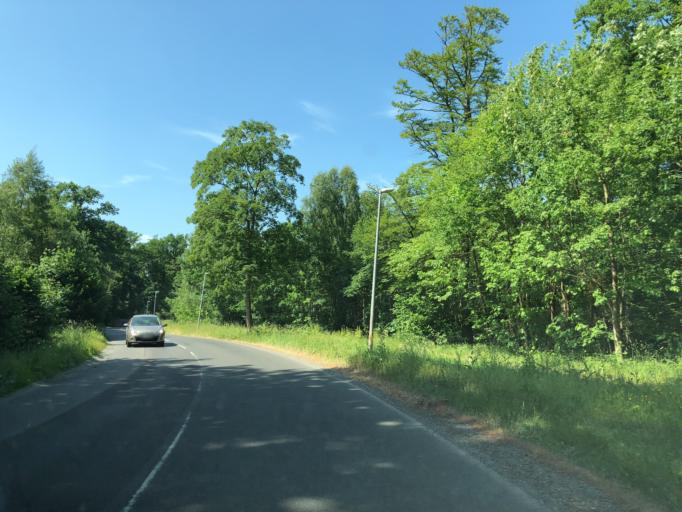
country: DK
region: South Denmark
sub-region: Kolding Kommune
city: Kolding
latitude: 55.5118
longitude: 9.4927
